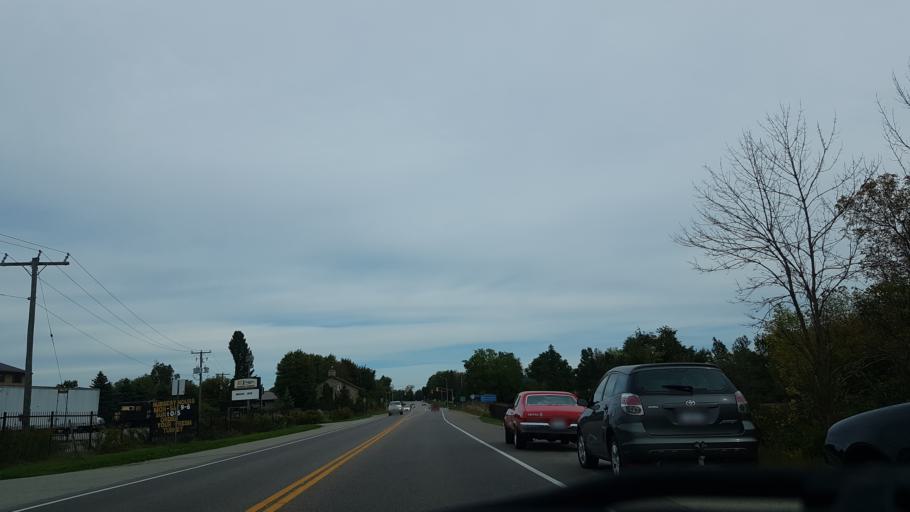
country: CA
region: Ontario
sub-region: Wellington County
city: Guelph
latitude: 43.6156
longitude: -80.2184
